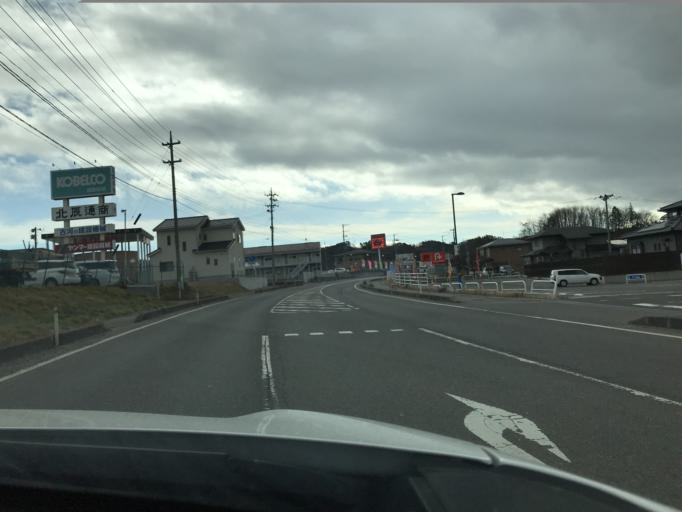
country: JP
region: Fukushima
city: Funehikimachi-funehiki
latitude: 37.4338
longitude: 140.5940
